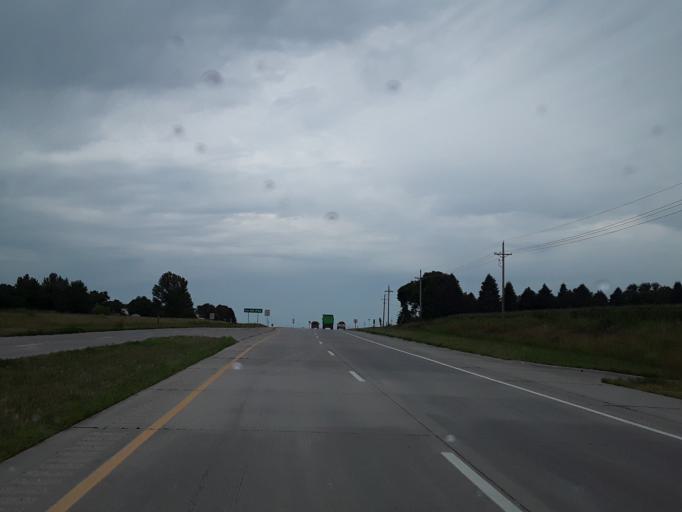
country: US
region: Nebraska
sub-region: Washington County
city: Blair
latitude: 41.4994
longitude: -96.1476
